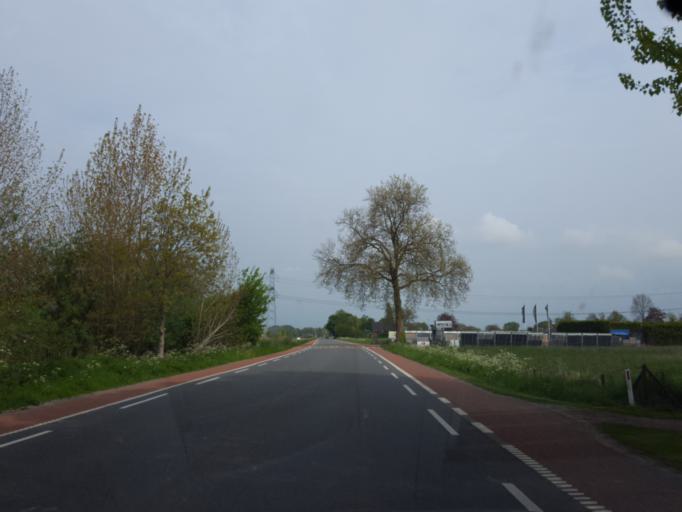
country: NL
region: Gelderland
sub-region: Gemeente Druten
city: Druten
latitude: 51.8841
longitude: 5.6362
